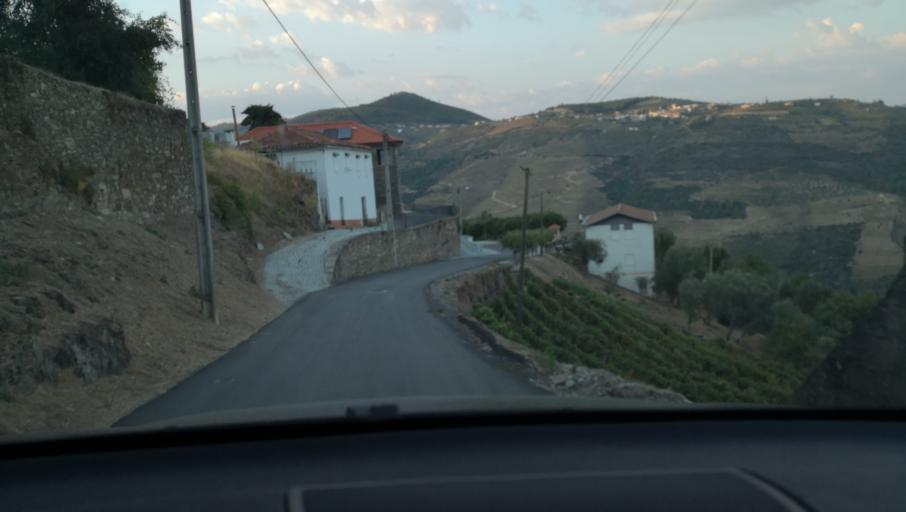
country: PT
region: Vila Real
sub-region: Sabrosa
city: Vilela
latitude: 41.1979
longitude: -7.5741
